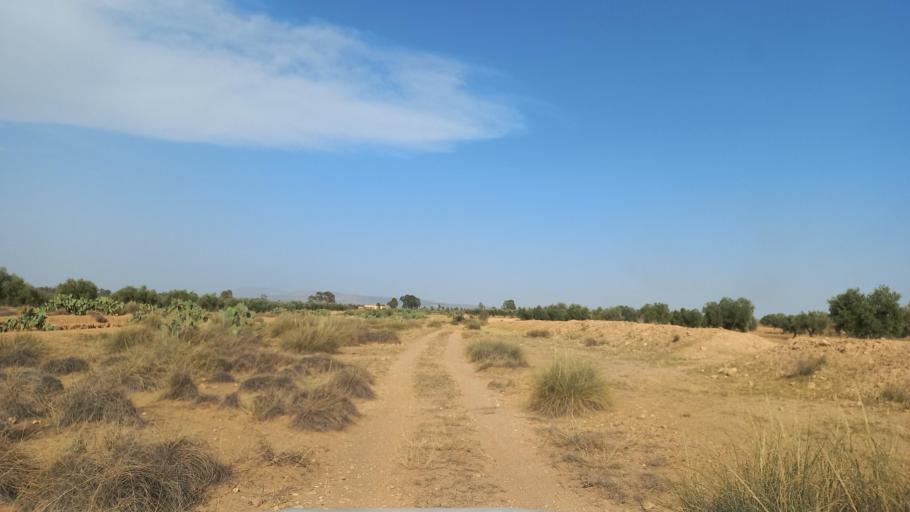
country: TN
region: Al Qasrayn
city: Kasserine
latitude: 35.2230
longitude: 8.9631
